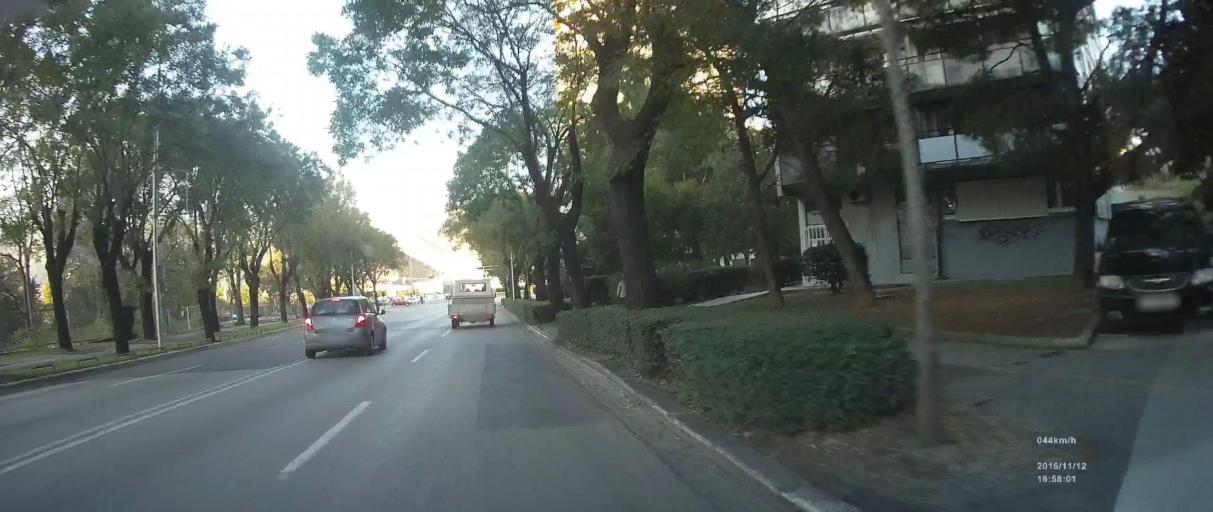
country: HR
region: Splitsko-Dalmatinska
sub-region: Grad Split
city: Split
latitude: 43.5155
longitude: 16.4293
